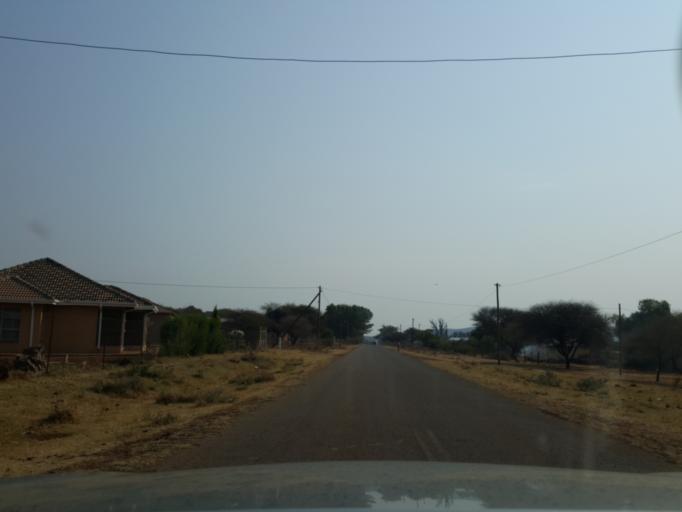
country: BW
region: South East
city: Lobatse
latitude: -25.3221
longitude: 25.7941
